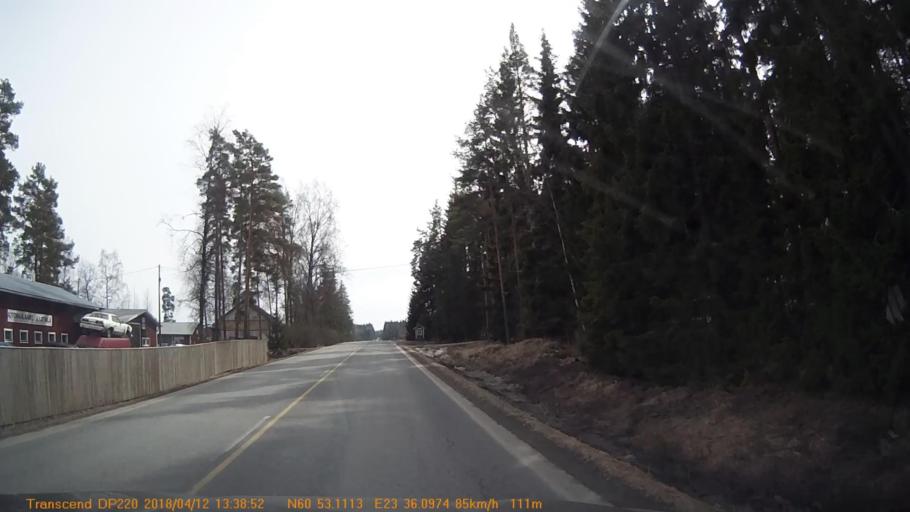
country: FI
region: Haeme
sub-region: Forssa
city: Forssa
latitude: 60.8849
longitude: 23.6017
